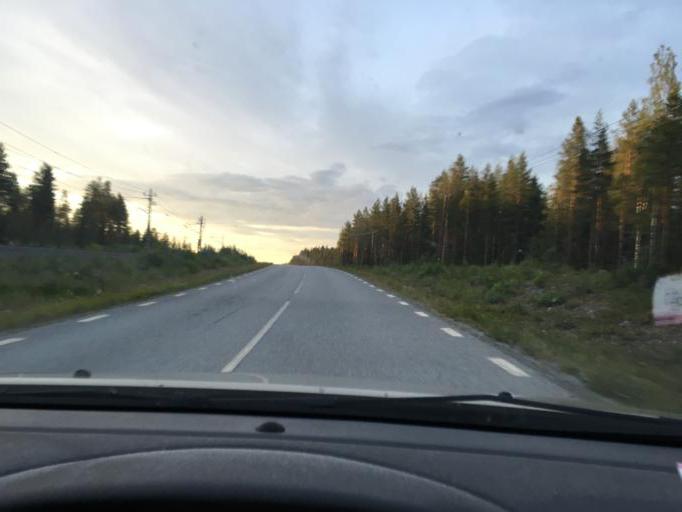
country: SE
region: Norrbotten
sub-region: Lulea Kommun
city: Ranea
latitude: 66.0407
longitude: 22.3360
